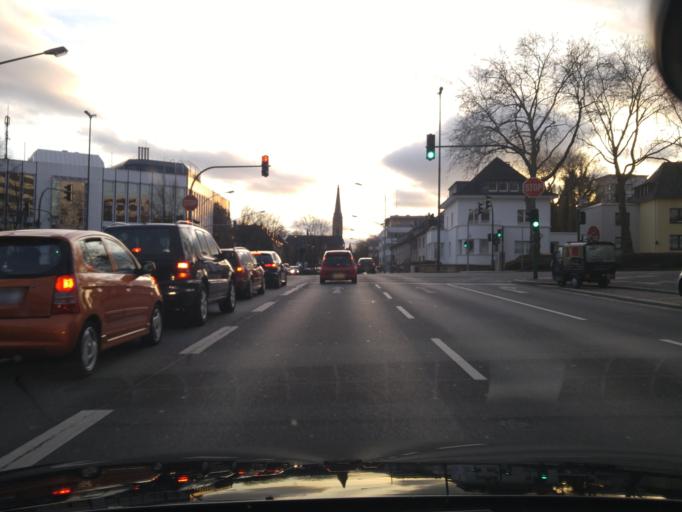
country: DE
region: North Rhine-Westphalia
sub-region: Regierungsbezirk Dusseldorf
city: Essen
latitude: 51.4432
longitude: 7.0341
